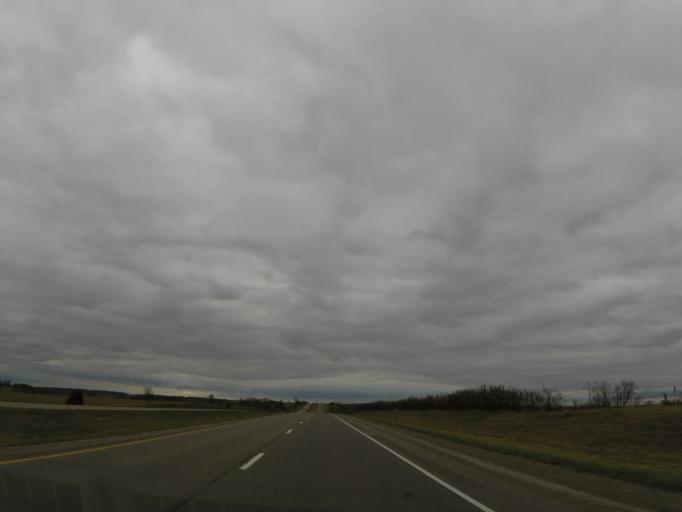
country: US
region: Iowa
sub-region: Washington County
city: Washington
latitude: 41.3701
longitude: -91.5516
